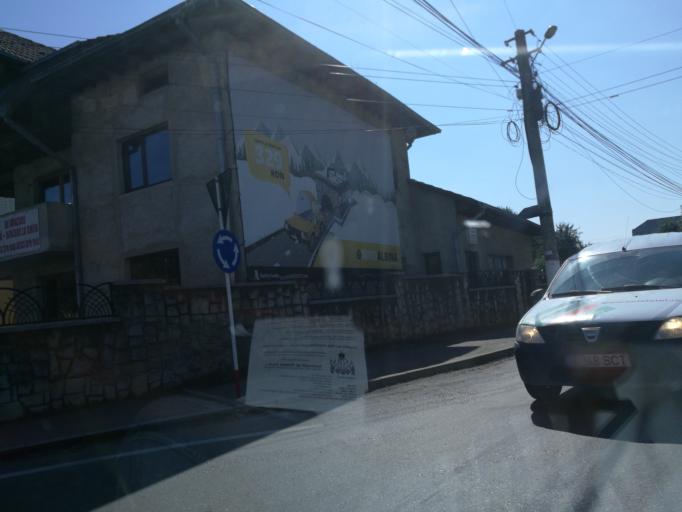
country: RO
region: Suceava
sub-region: Municipiul Suceava
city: Radauti
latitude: 47.8408
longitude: 25.9241
